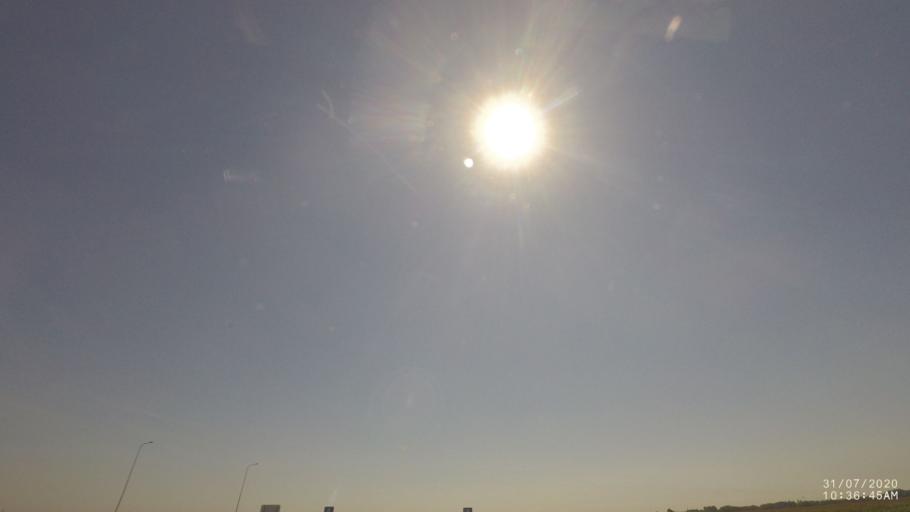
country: SK
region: Trnavsky
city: Dunajska Streda
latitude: 48.0109
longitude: 17.4609
